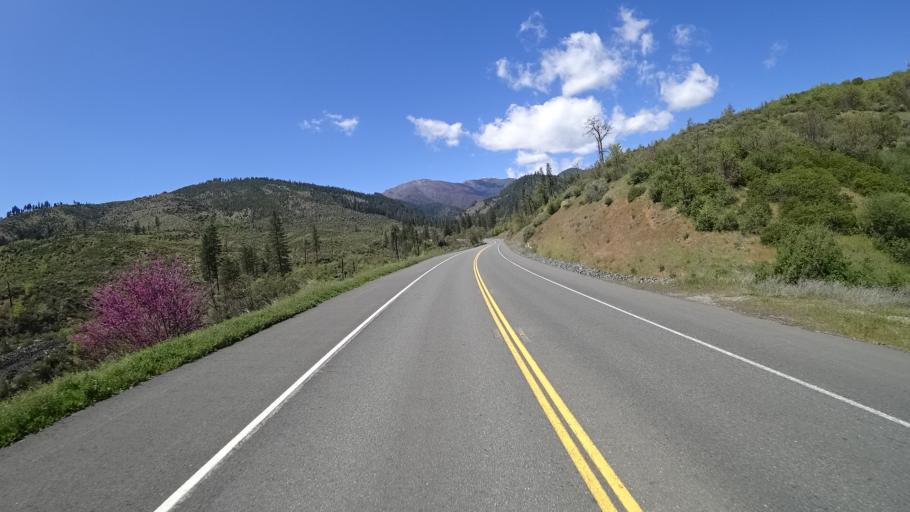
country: US
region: California
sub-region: Trinity County
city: Weaverville
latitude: 40.7389
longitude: -122.9667
